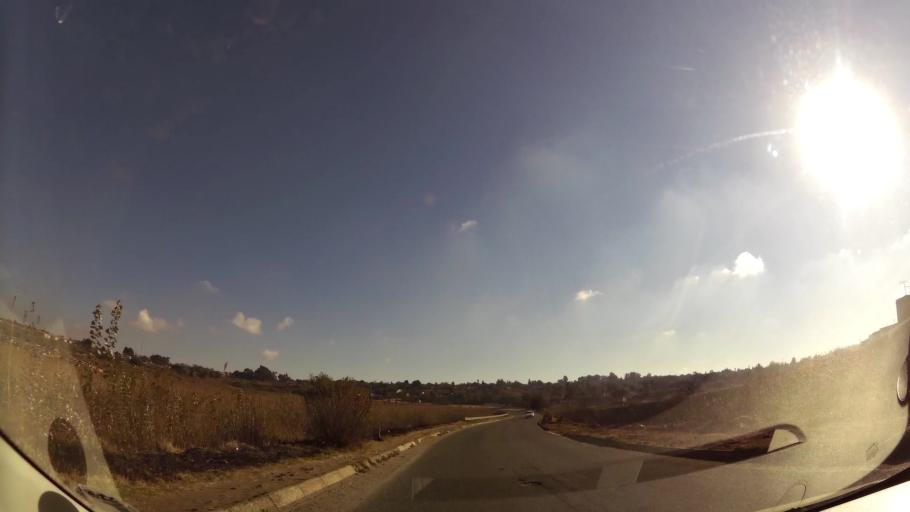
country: ZA
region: Gauteng
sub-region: City of Johannesburg Metropolitan Municipality
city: Roodepoort
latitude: -26.1563
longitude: 27.8434
